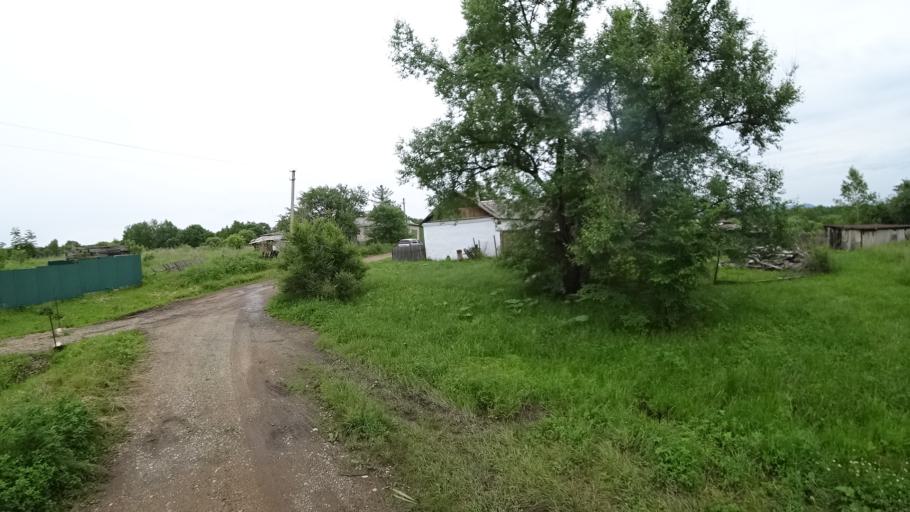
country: RU
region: Primorskiy
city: Novosysoyevka
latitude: 44.2070
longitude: 133.3266
